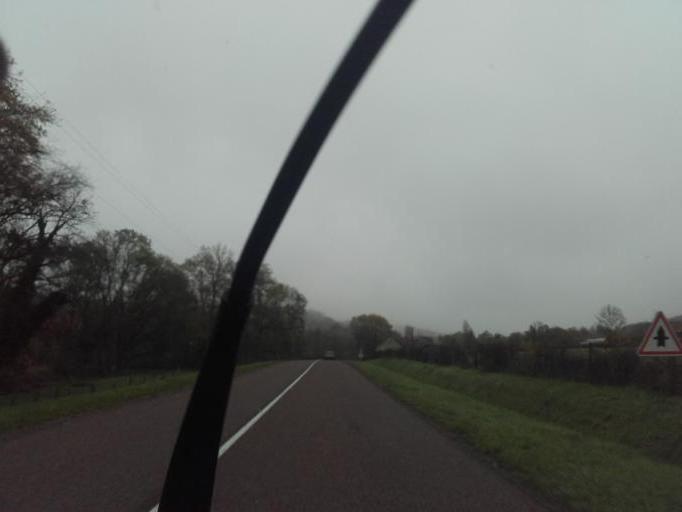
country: FR
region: Bourgogne
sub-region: Departement de la Cote-d'Or
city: Nuits-Saint-Georges
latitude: 47.1426
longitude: 4.9062
